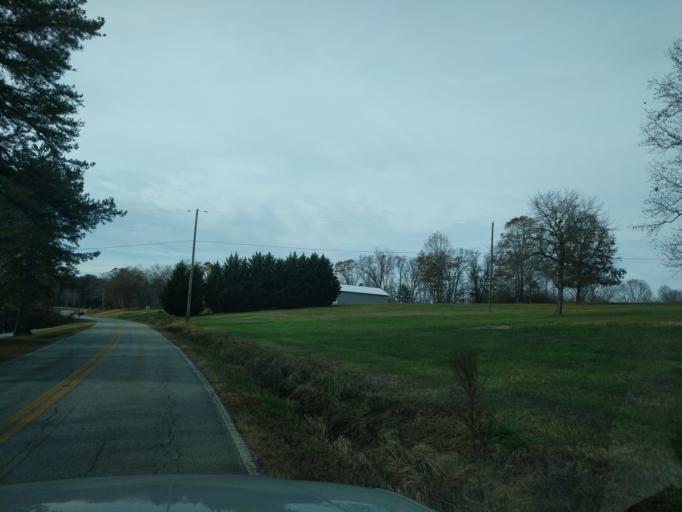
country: US
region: South Carolina
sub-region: Oconee County
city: Walhalla
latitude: 34.8312
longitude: -83.0478
